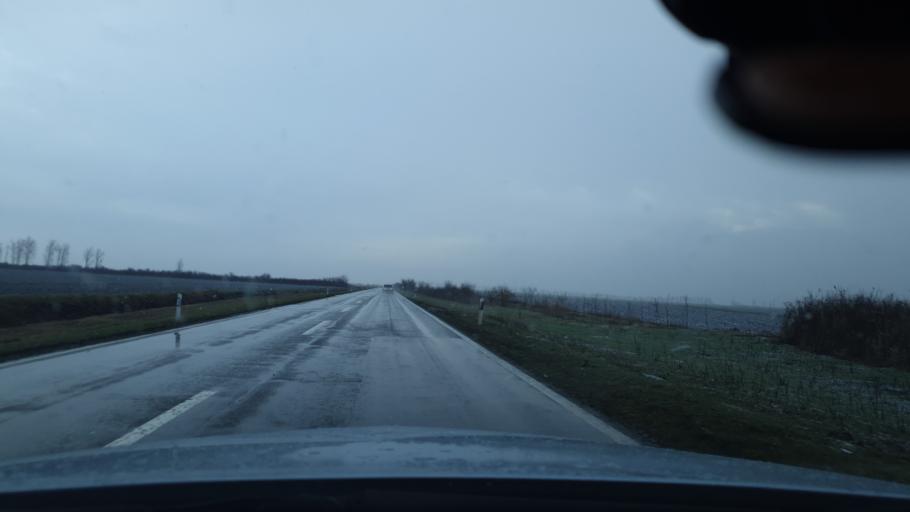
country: RS
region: Autonomna Pokrajina Vojvodina
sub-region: Juznobanatski Okrug
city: Pancevo
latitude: 44.8508
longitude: 20.7707
